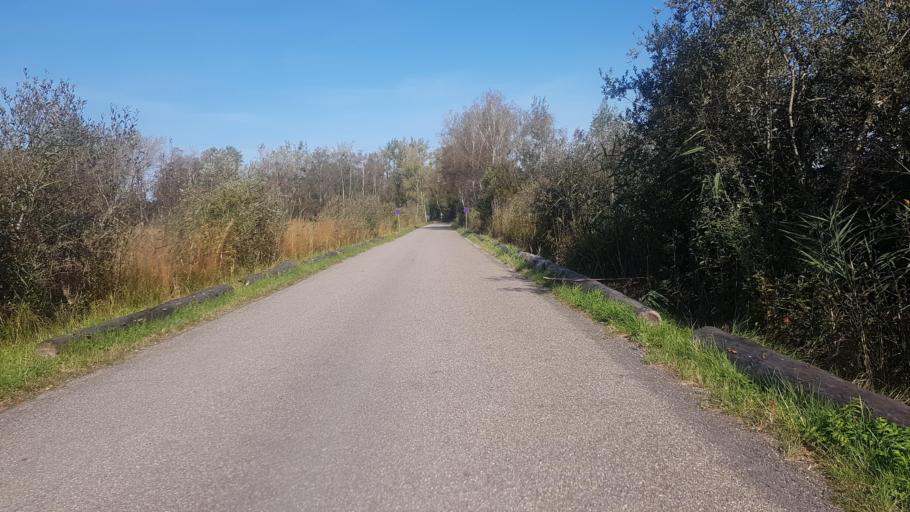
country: AT
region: Vorarlberg
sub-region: Politischer Bezirk Bregenz
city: Hochst
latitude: 47.4935
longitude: 9.6276
